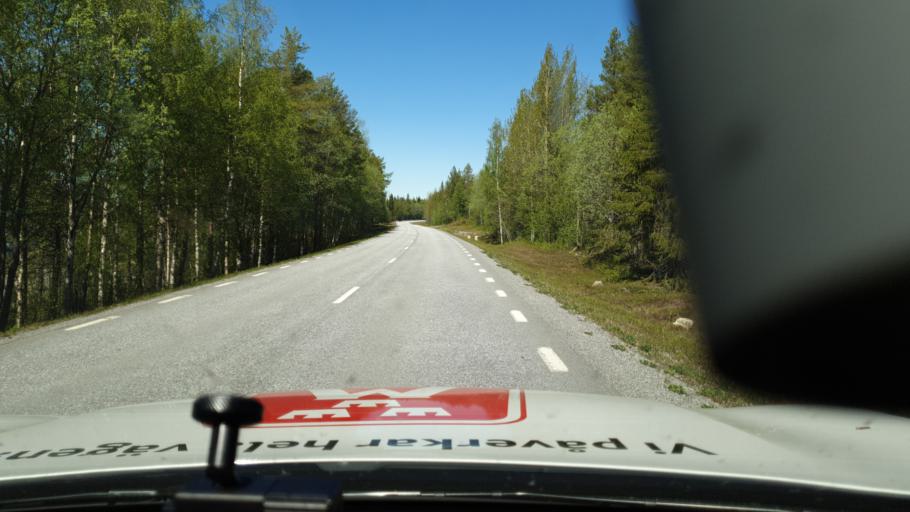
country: SE
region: Vaesterbotten
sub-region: Storumans Kommun
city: Storuman
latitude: 65.1752
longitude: 17.0241
